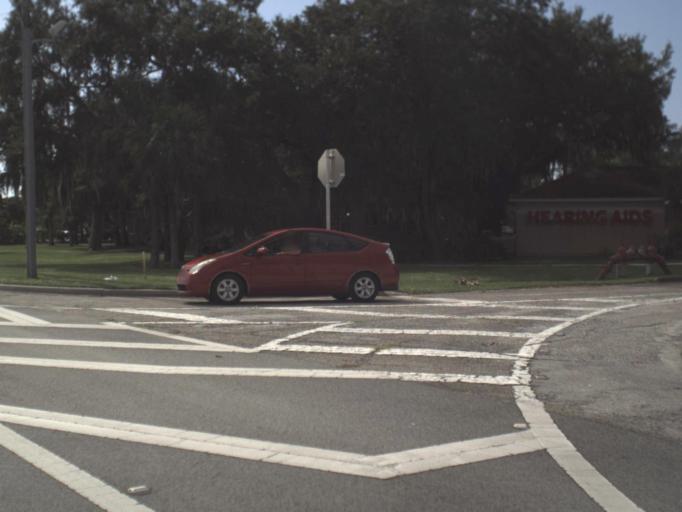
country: US
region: Florida
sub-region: Charlotte County
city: Port Charlotte
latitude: 27.0086
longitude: -82.1372
